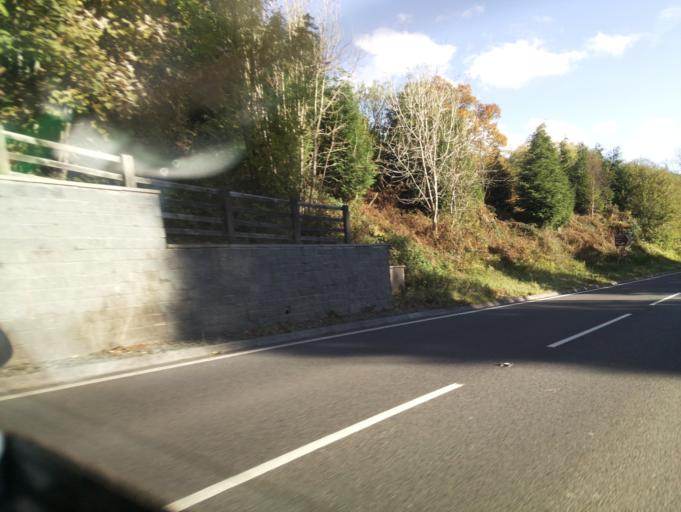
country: GB
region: Wales
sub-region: Rhondda Cynon Taf
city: Hirwaun
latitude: 51.8256
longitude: -3.4500
